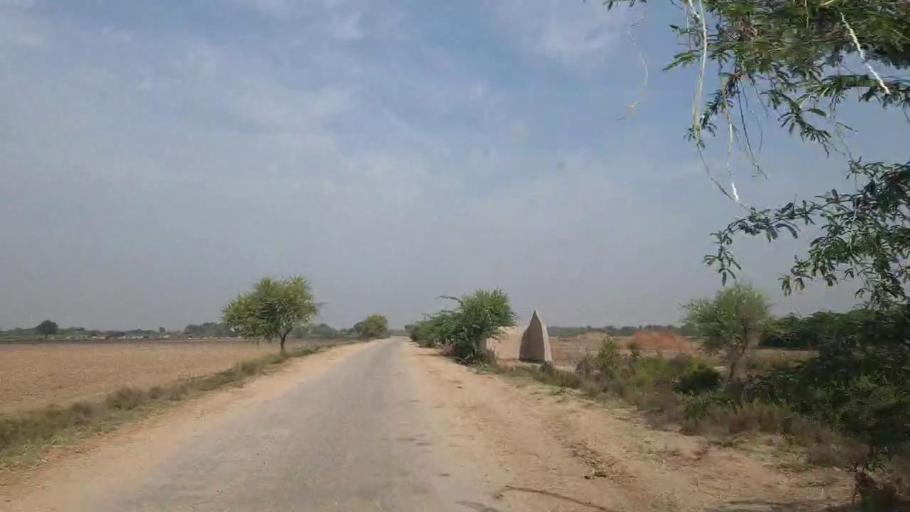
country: PK
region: Sindh
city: Tando Bago
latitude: 24.9311
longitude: 68.9879
